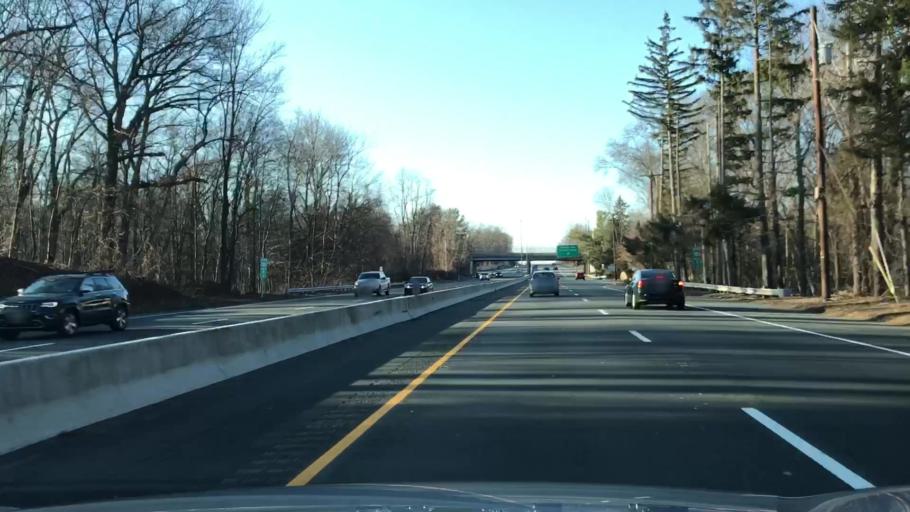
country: US
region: New Jersey
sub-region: Bergen County
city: Franklin Lakes
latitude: 41.0105
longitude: -74.1999
